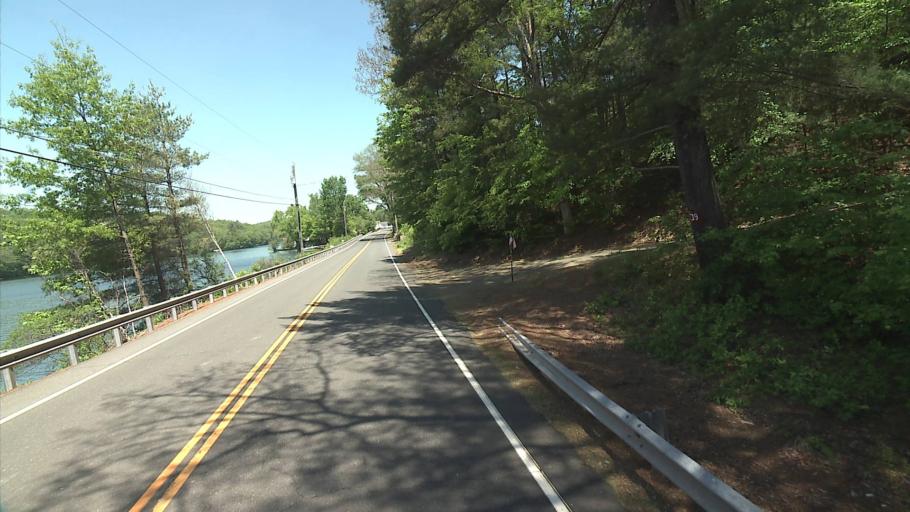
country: US
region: Connecticut
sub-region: Tolland County
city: Stafford
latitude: 42.0040
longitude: -72.2559
